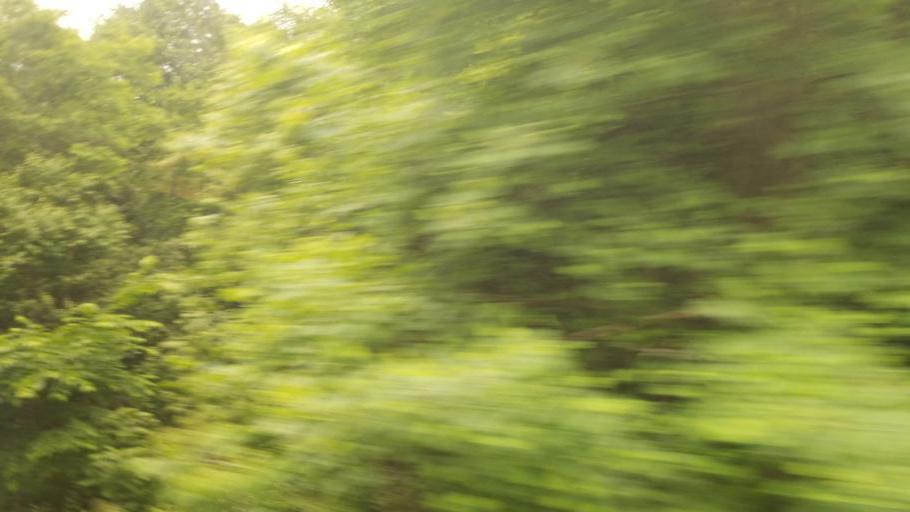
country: US
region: Pennsylvania
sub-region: Somerset County
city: Milford
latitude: 39.8280
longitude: -79.3074
